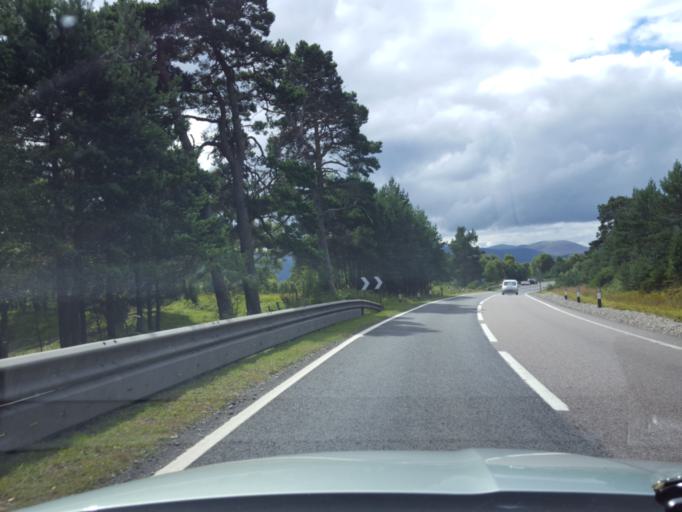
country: GB
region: Scotland
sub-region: Highland
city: Aviemore
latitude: 57.2200
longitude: -3.8146
